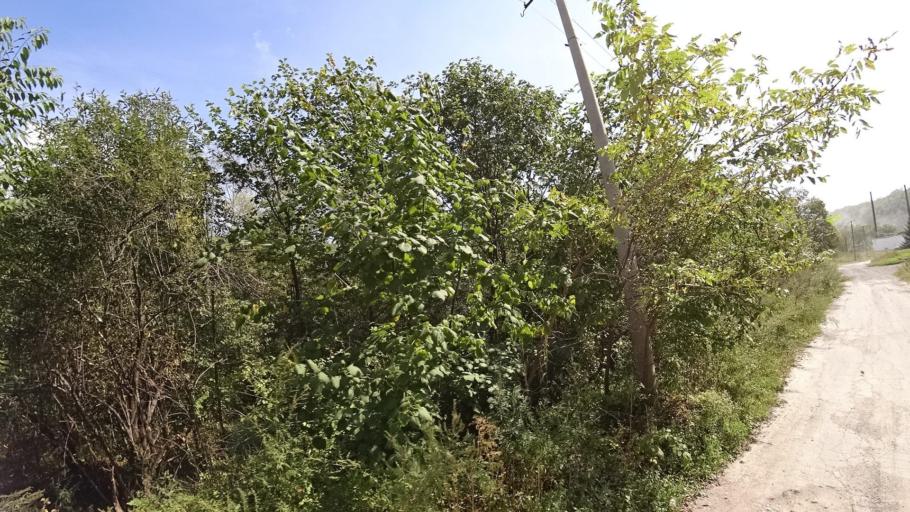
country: RU
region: Jewish Autonomous Oblast
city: Londoko
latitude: 49.0254
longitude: 131.9261
